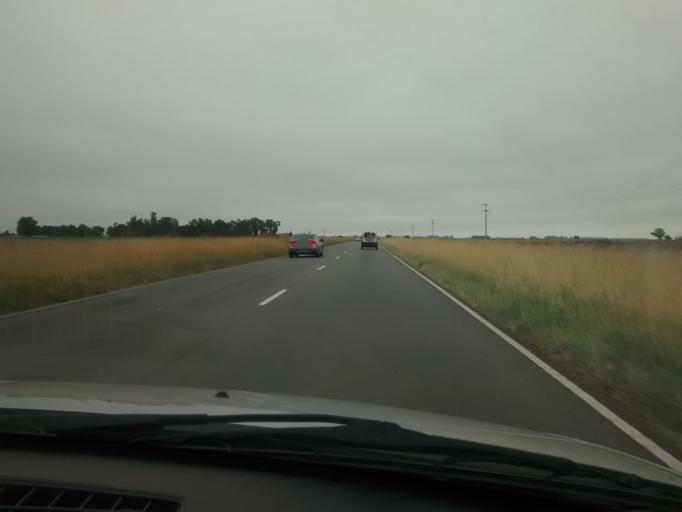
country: AR
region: Buenos Aires
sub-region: Partido de Ayacucho
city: Ayacucho
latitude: -37.0521
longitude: -58.5423
